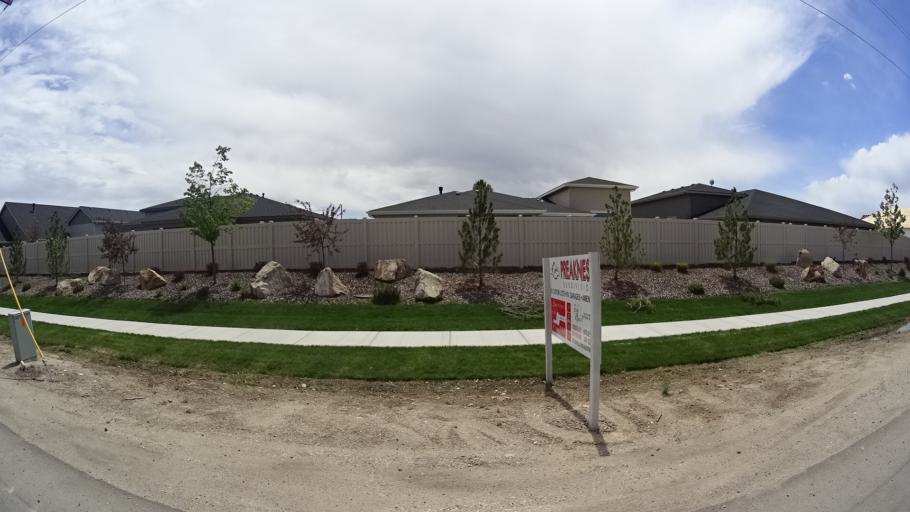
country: US
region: Idaho
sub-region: Ada County
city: Meridian
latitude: 43.5756
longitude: -116.4084
